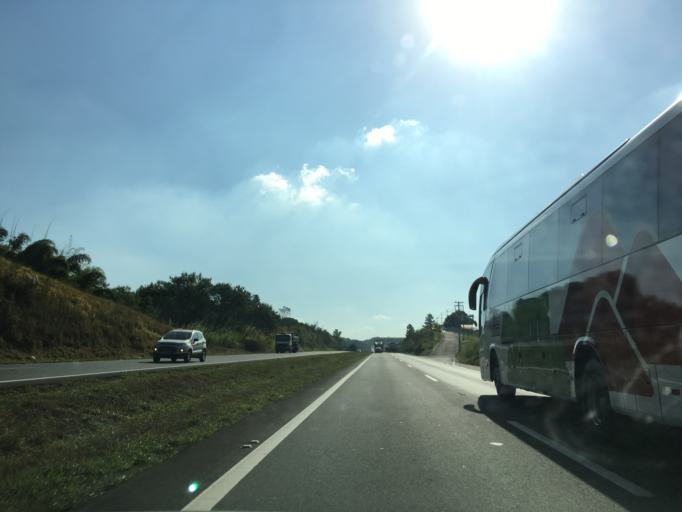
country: BR
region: Sao Paulo
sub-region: Piracicaba
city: Piracicaba
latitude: -22.7359
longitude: -47.5325
